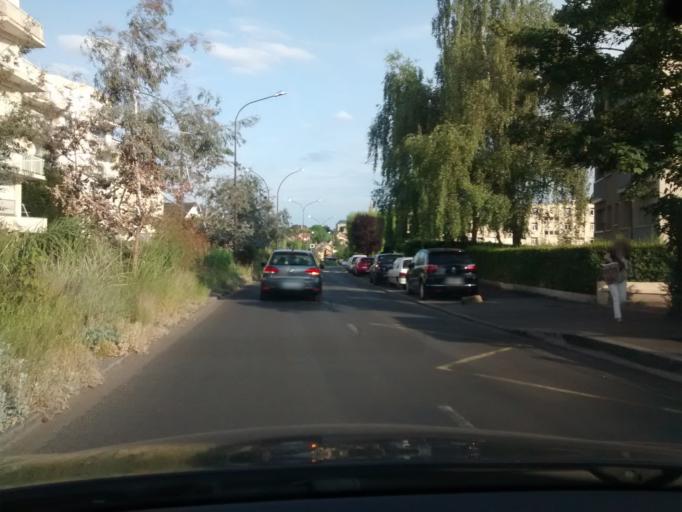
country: FR
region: Ile-de-France
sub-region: Departement des Yvelines
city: Le Chesnay
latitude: 48.8241
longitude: 2.1256
